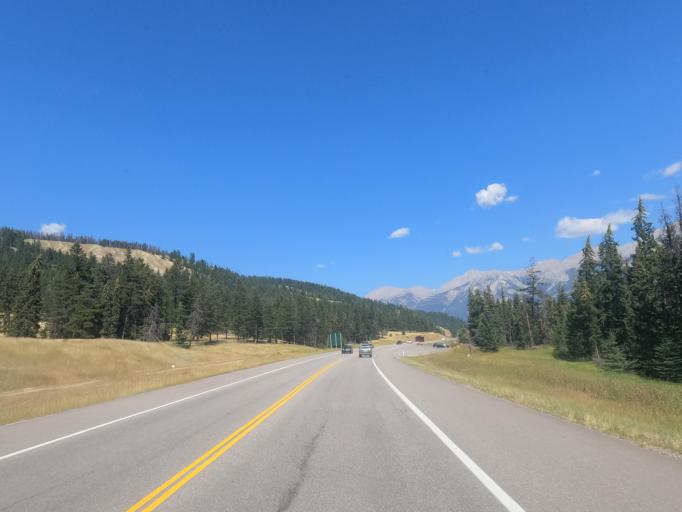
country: CA
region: Alberta
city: Jasper Park Lodge
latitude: 52.9032
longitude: -118.0653
